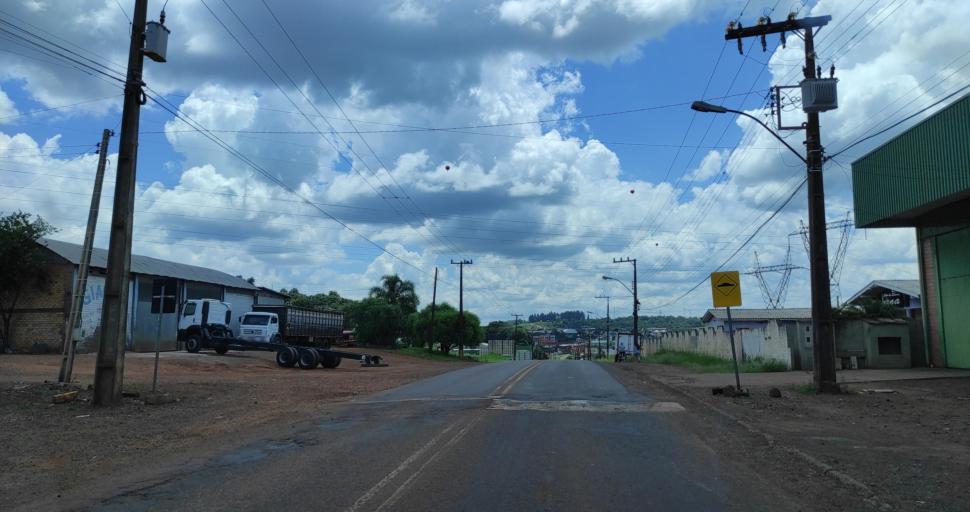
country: BR
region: Santa Catarina
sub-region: Xanxere
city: Xanxere
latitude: -26.8661
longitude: -52.4095
